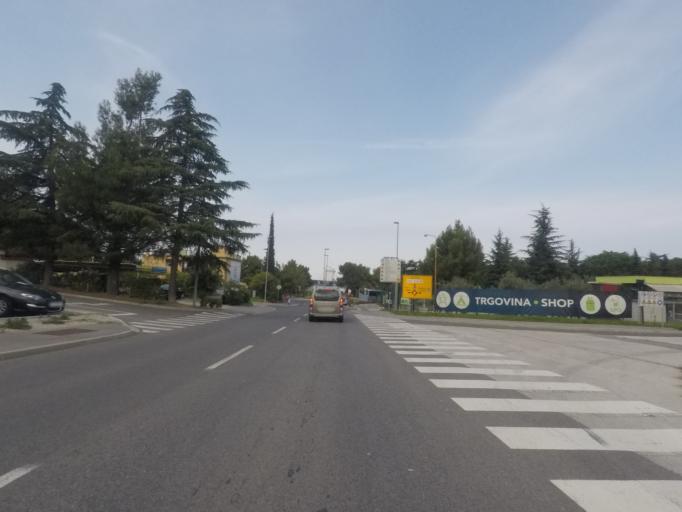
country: SI
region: Izola-Isola
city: Izola
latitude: 45.5375
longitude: 13.6702
